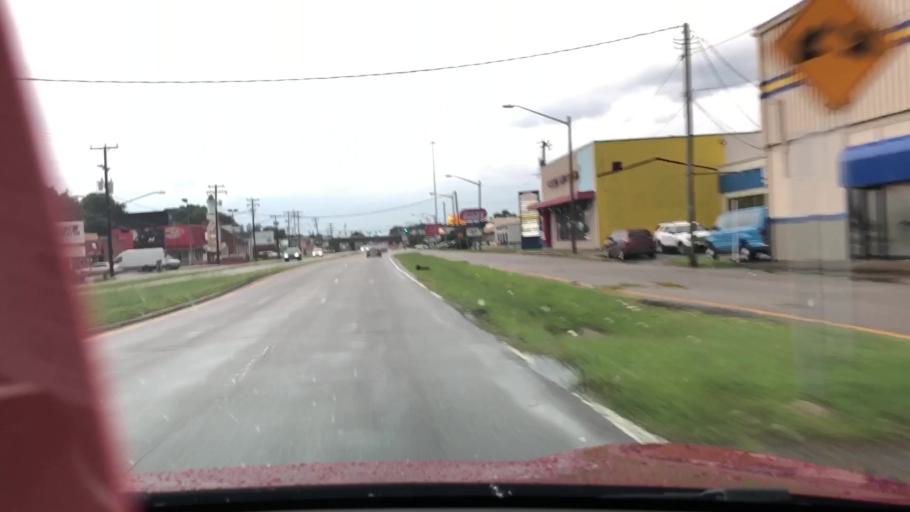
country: US
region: Virginia
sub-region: City of Chesapeake
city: Chesapeake
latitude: 36.8555
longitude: -76.2008
